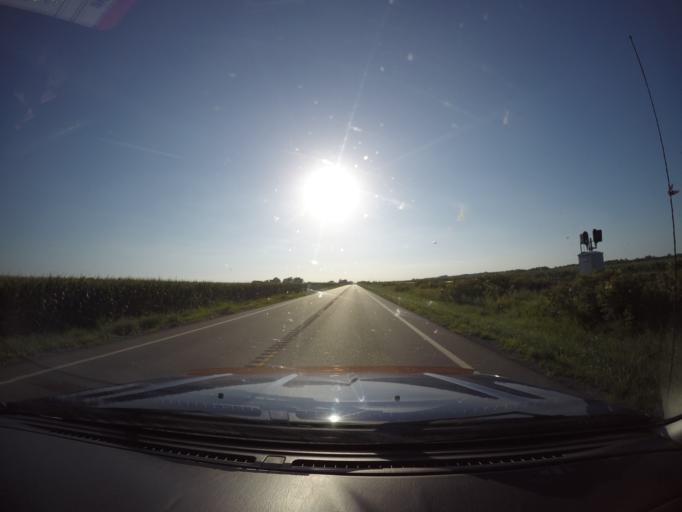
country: US
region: Kansas
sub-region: Shawnee County
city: Silver Lake
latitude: 39.1114
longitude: -95.8841
